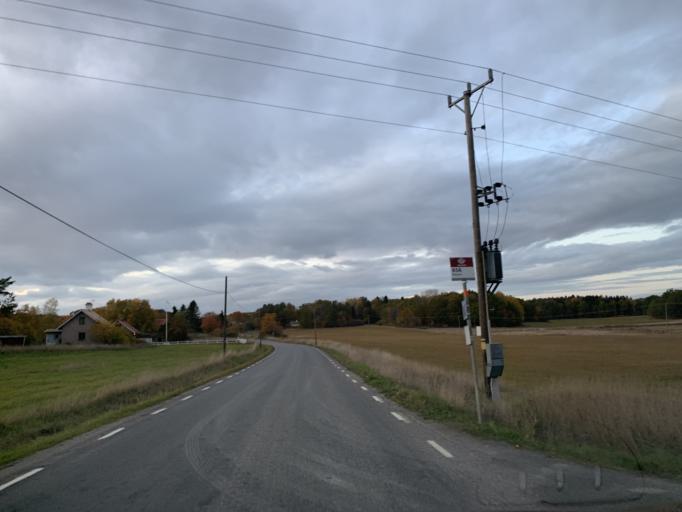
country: SE
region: Stockholm
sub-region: Nynashamns Kommun
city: Osmo
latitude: 58.9237
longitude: 17.7746
